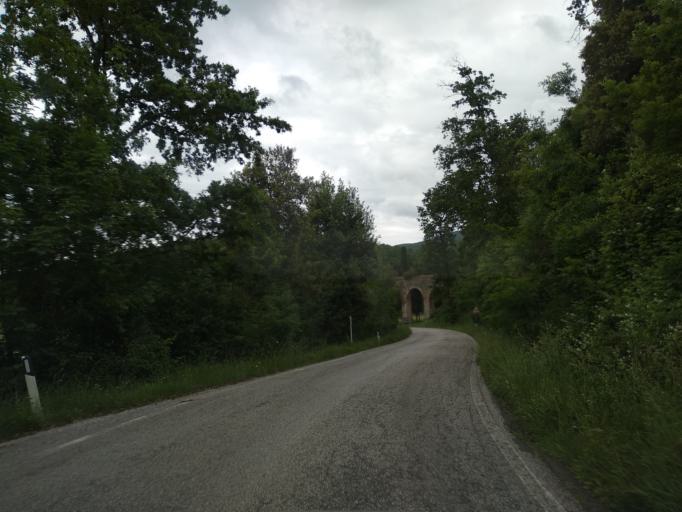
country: IT
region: Tuscany
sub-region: Provincia di Livorno
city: Guasticce
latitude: 43.5642
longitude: 10.4245
